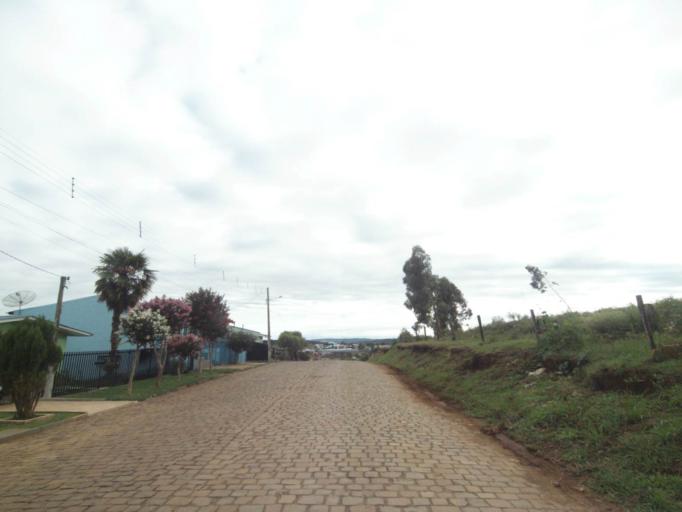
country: BR
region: Rio Grande do Sul
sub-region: Lagoa Vermelha
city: Lagoa Vermelha
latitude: -28.2178
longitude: -51.5131
